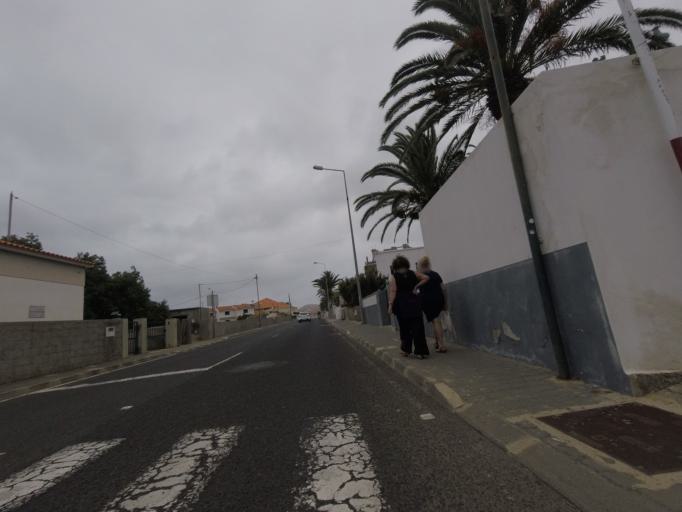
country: PT
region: Madeira
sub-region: Porto Santo
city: Vila de Porto Santo
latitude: 33.0495
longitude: -16.3516
